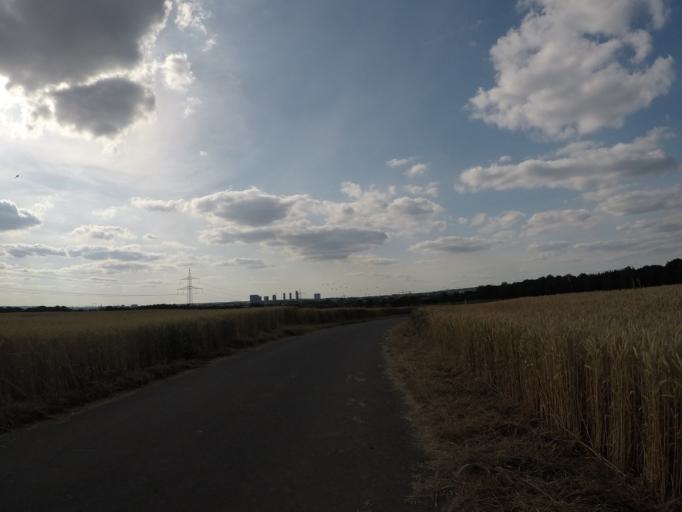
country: LU
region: Luxembourg
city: Itzig
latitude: 49.6009
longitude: 6.1801
